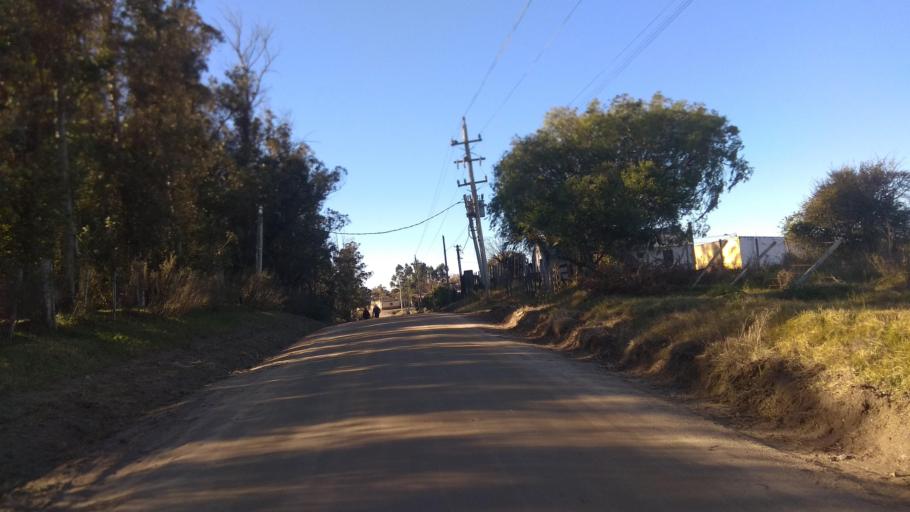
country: UY
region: Florida
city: Florida
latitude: -34.0948
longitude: -56.2424
